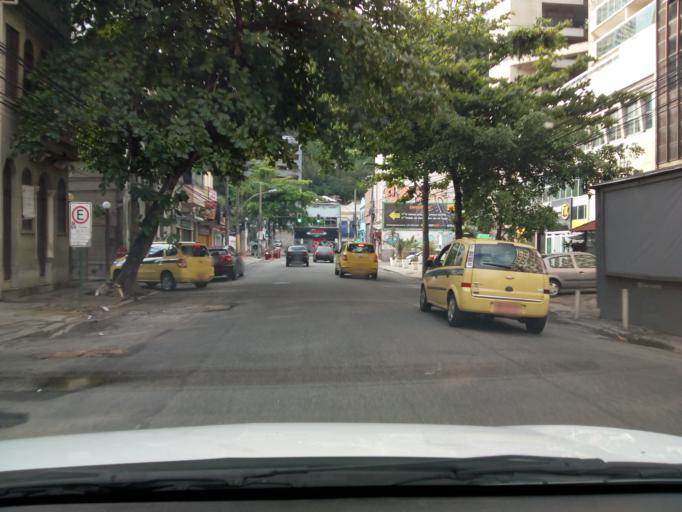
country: BR
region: Rio de Janeiro
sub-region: Rio De Janeiro
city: Rio de Janeiro
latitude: -22.9549
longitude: -43.1810
